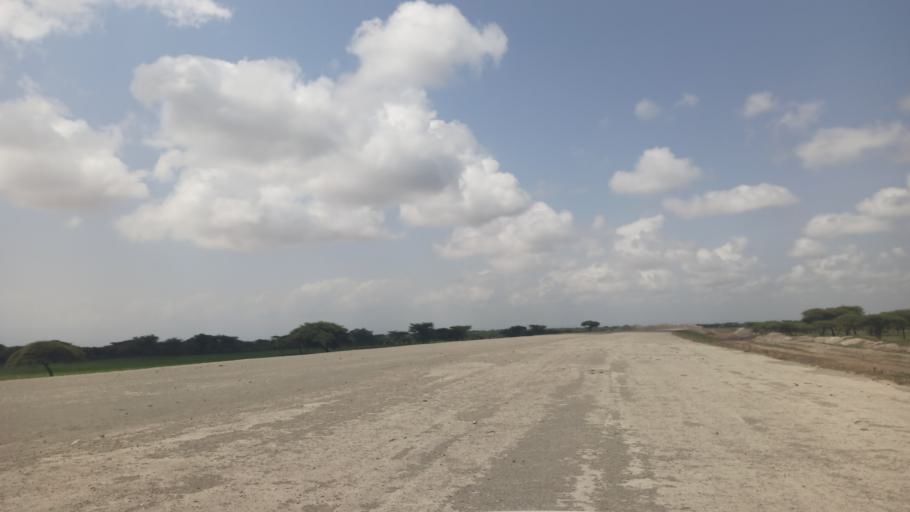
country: ET
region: Oromiya
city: Ziway
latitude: 7.6661
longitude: 38.6834
